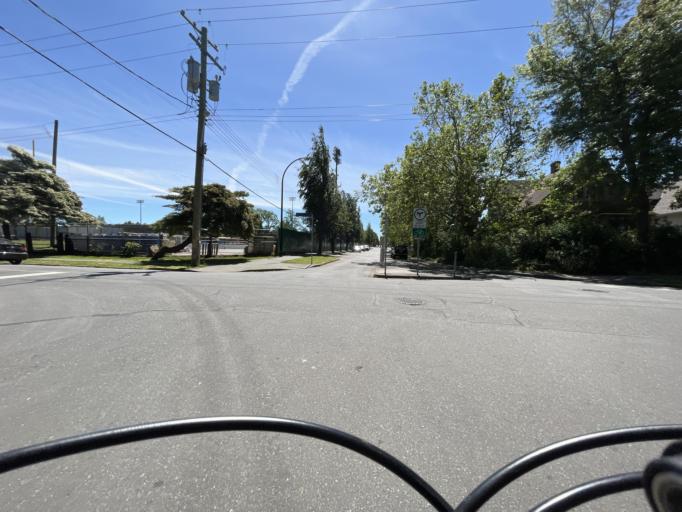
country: CA
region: British Columbia
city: Victoria
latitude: 48.4322
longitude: -123.3556
